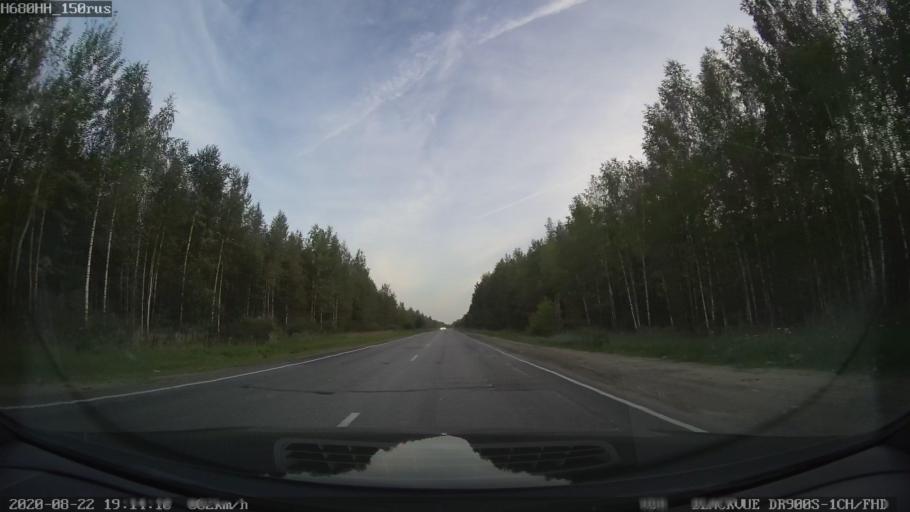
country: RU
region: Tverskaya
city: Sakharovo
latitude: 56.9824
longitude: 36.0236
